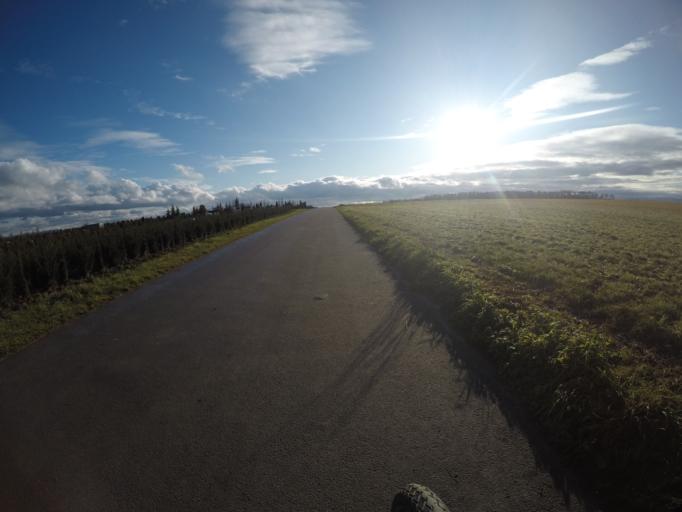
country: DE
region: Baden-Wuerttemberg
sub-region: Regierungsbezirk Stuttgart
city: Bondorf
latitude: 48.5482
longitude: 8.8745
